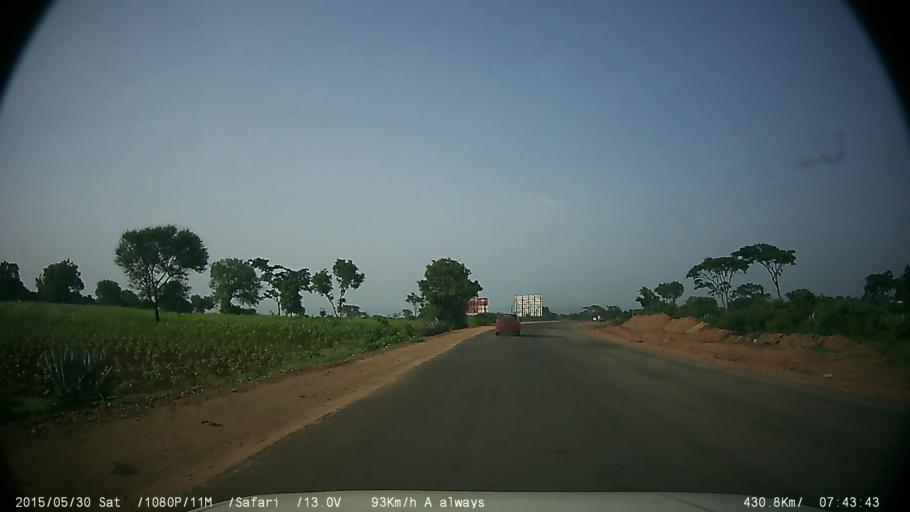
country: IN
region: Karnataka
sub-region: Chamrajnagar
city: Gundlupet
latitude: 11.9043
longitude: 76.6721
